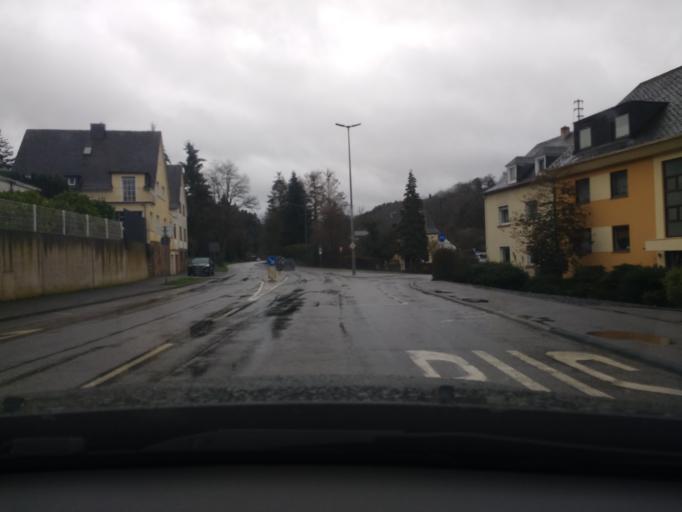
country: DE
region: Rheinland-Pfalz
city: Irsch
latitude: 49.7404
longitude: 6.6731
